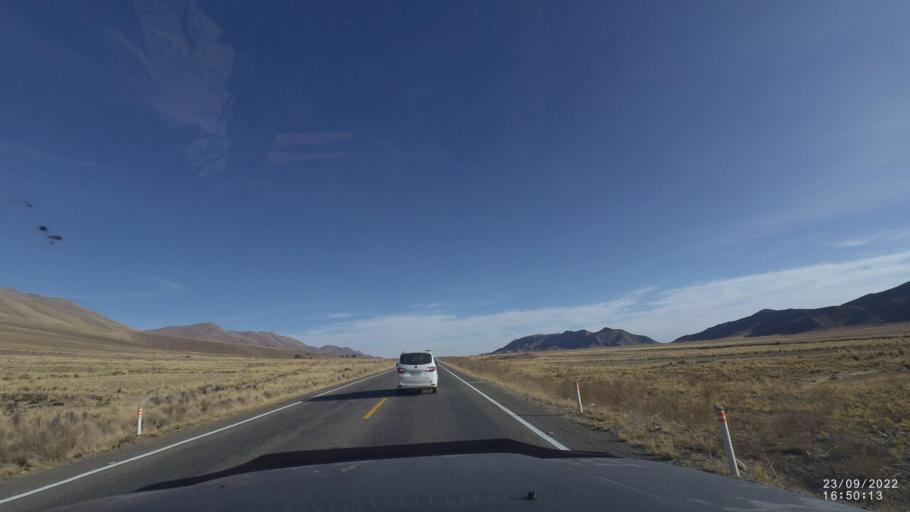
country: BO
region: Oruro
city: Poopo
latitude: -18.3998
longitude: -66.9775
